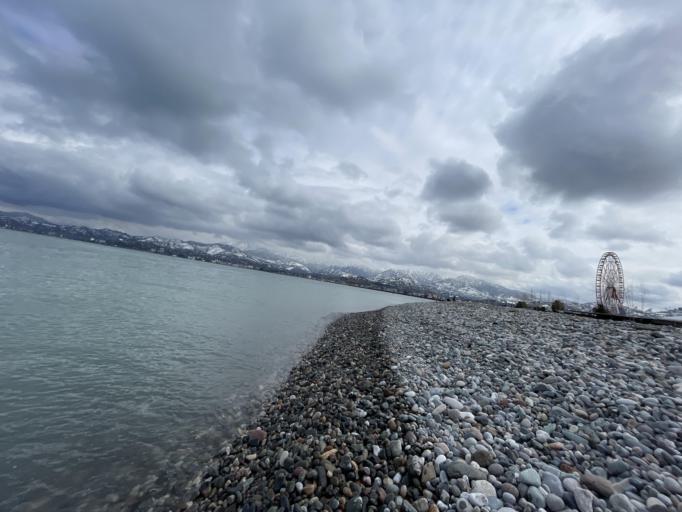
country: GE
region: Ajaria
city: Batumi
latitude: 41.6577
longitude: 41.6411
